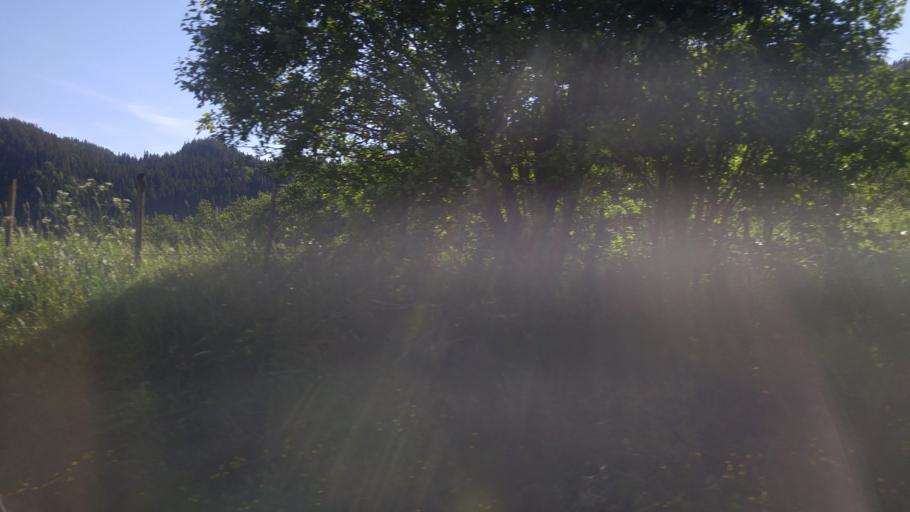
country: NO
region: Sor-Trondelag
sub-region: Melhus
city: Lundamo
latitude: 63.1915
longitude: 10.2991
